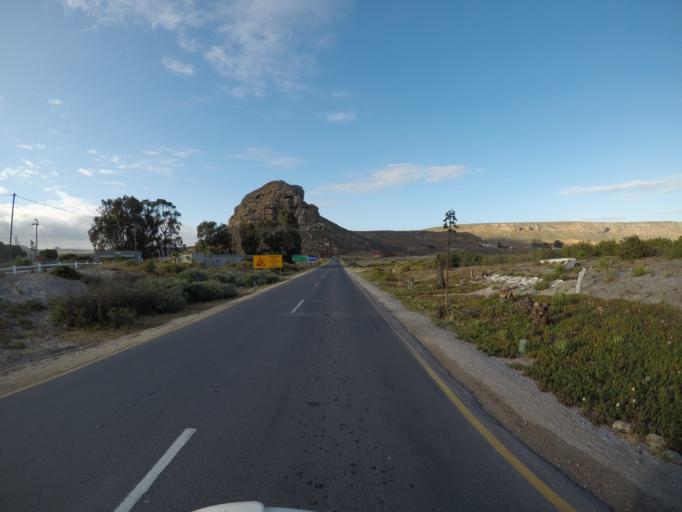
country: ZA
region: Western Cape
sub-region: West Coast District Municipality
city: Clanwilliam
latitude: -32.3132
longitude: 18.3554
